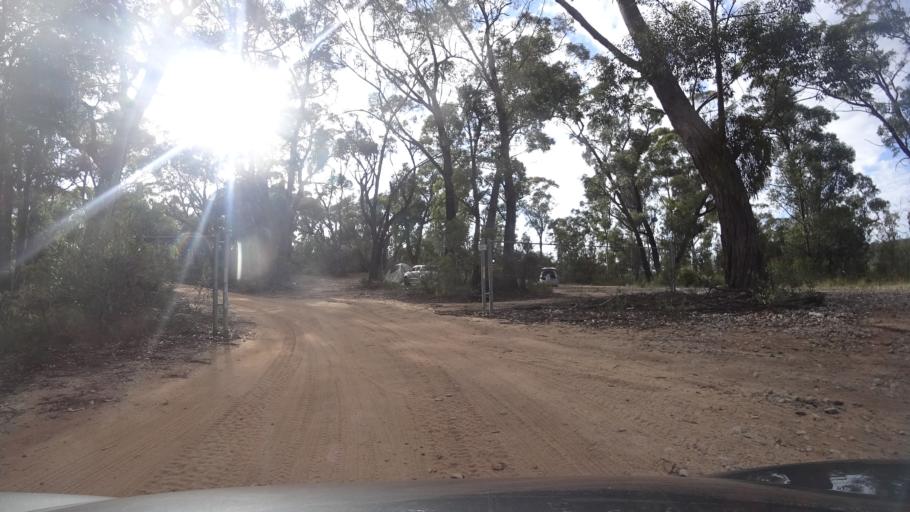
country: AU
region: New South Wales
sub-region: Lithgow
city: Lithgow
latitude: -33.4836
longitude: 150.2458
